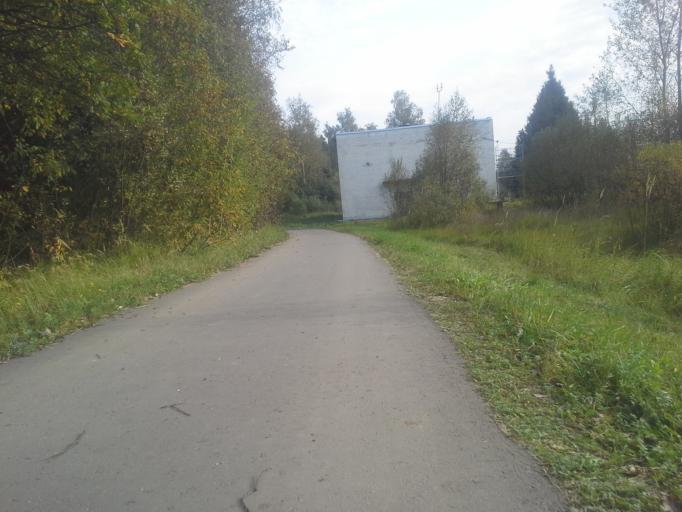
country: RU
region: Moskovskaya
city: Kievskij
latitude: 55.3856
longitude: 36.9095
